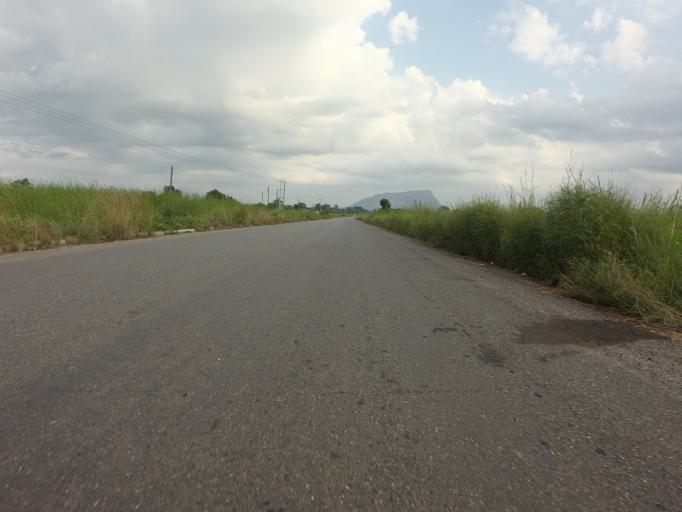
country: GH
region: Volta
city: Ho
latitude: 6.5735
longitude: 0.4844
